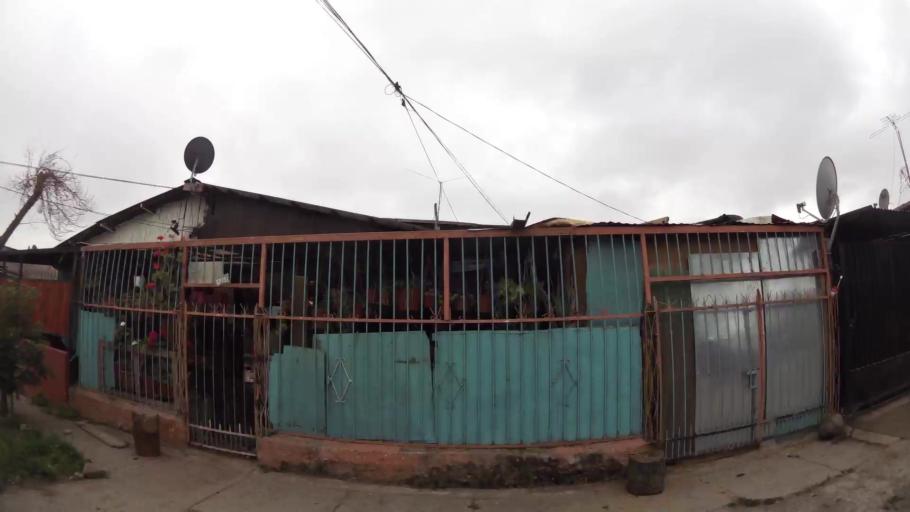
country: CL
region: Santiago Metropolitan
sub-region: Provincia de Maipo
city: San Bernardo
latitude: -33.5264
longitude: -70.6899
